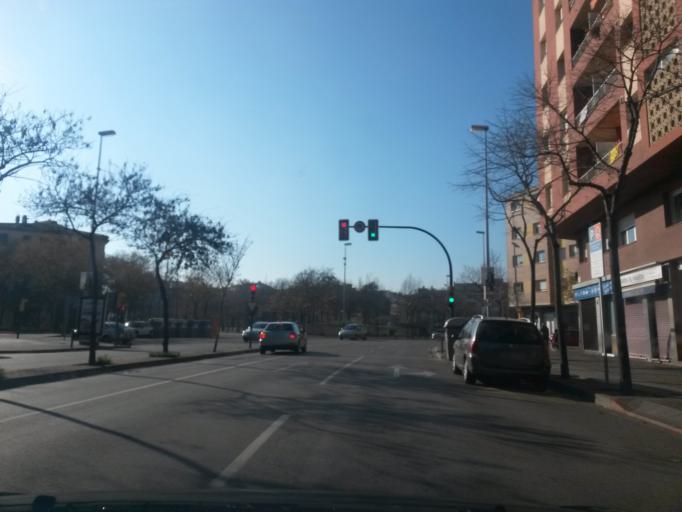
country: ES
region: Catalonia
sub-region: Provincia de Girona
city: Salt
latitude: 41.9753
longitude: 2.8065
